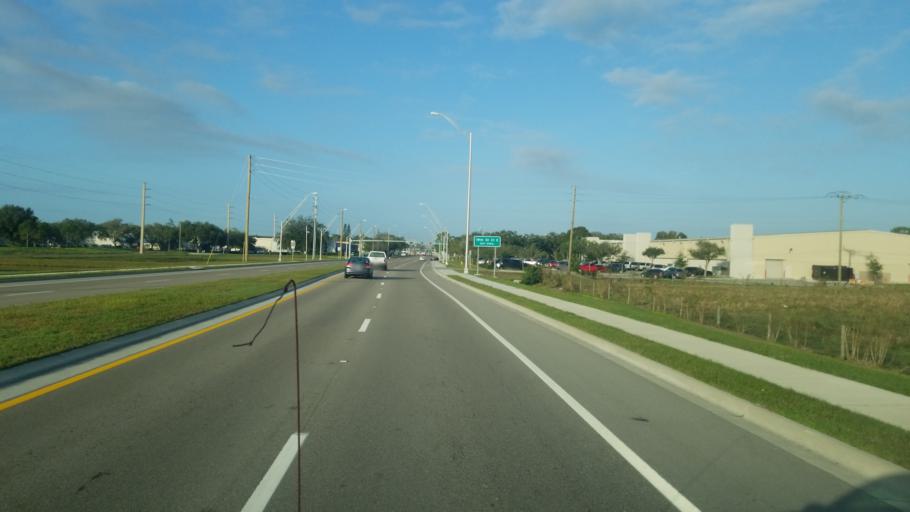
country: US
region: Florida
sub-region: Manatee County
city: Samoset
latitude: 27.4623
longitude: -82.5373
